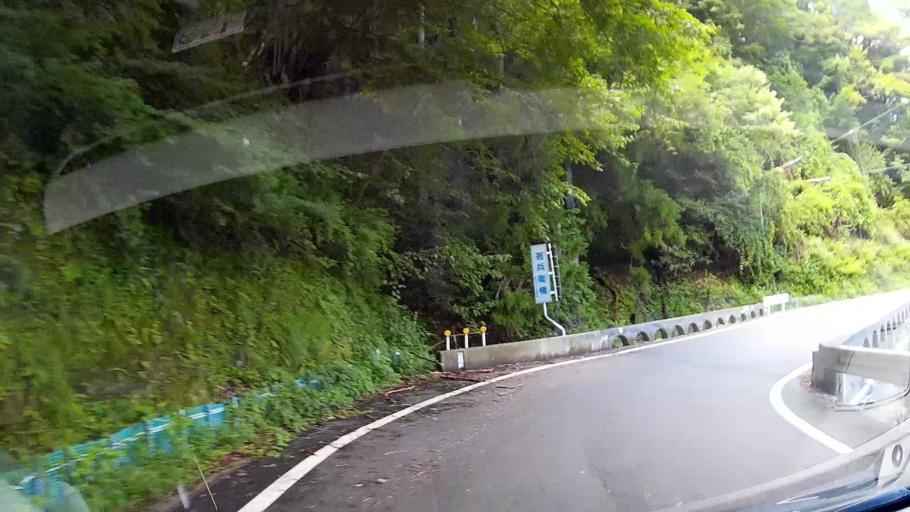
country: JP
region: Shizuoka
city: Shizuoka-shi
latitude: 35.2314
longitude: 138.2513
